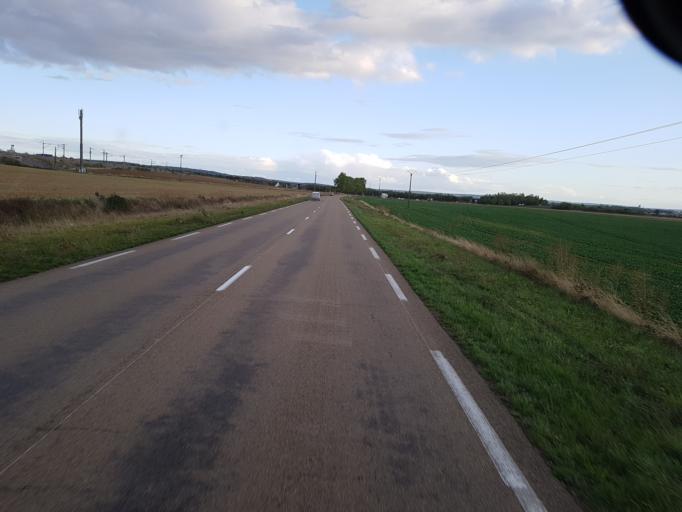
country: FR
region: Bourgogne
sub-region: Departement de l'Yonne
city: Soucy
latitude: 48.2655
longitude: 3.2797
